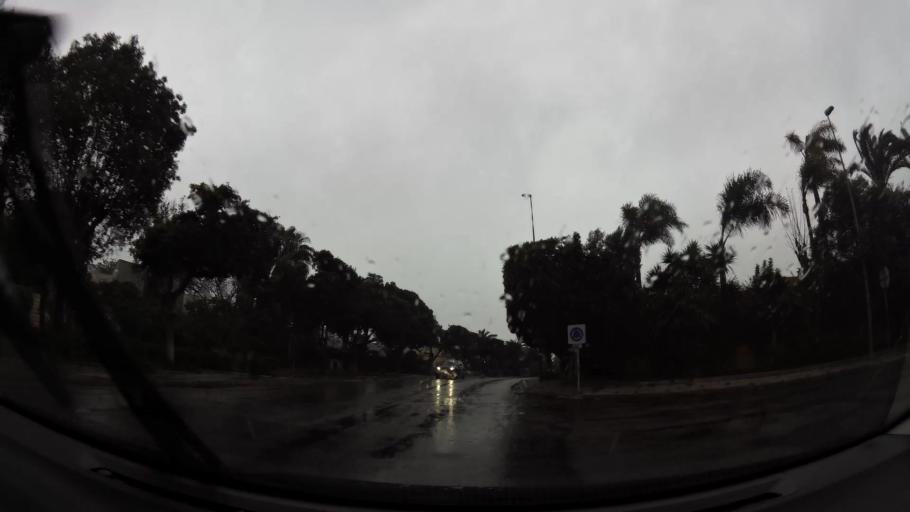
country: MA
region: Grand Casablanca
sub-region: Casablanca
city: Casablanca
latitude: 33.5857
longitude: -7.6674
